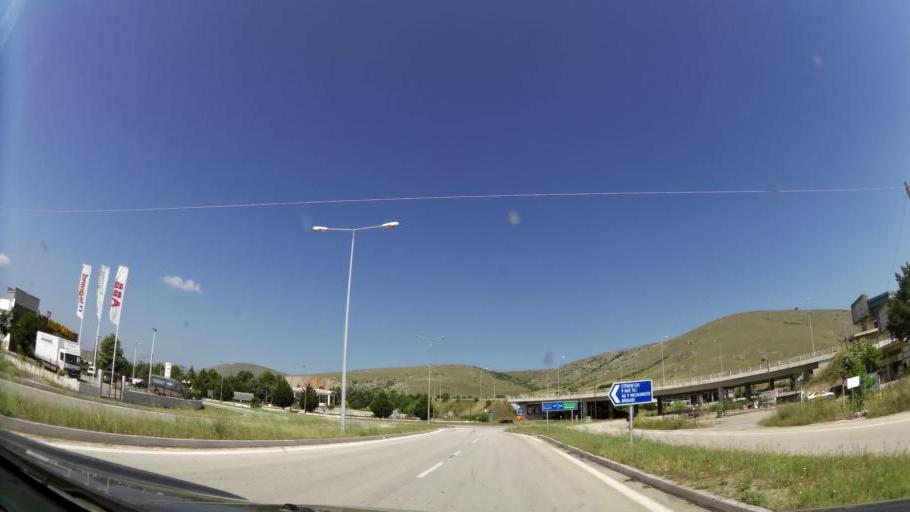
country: GR
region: West Macedonia
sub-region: Nomos Kozanis
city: Koila
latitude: 40.3454
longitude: 21.7999
